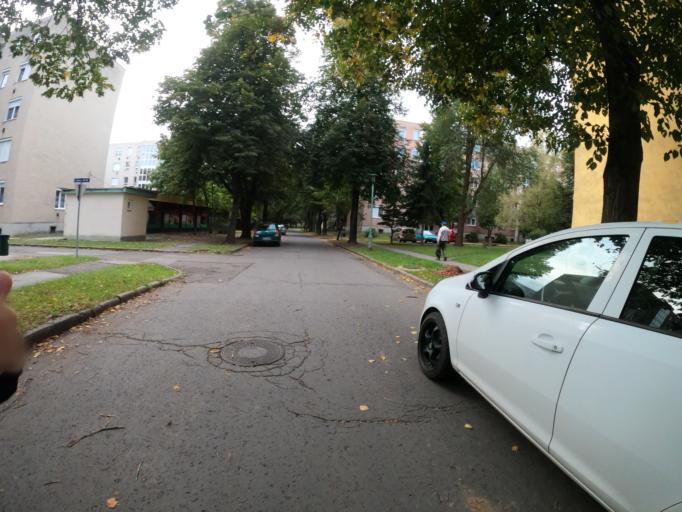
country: HU
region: Borsod-Abauj-Zemplen
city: Sajobabony
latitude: 48.0968
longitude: 20.7084
